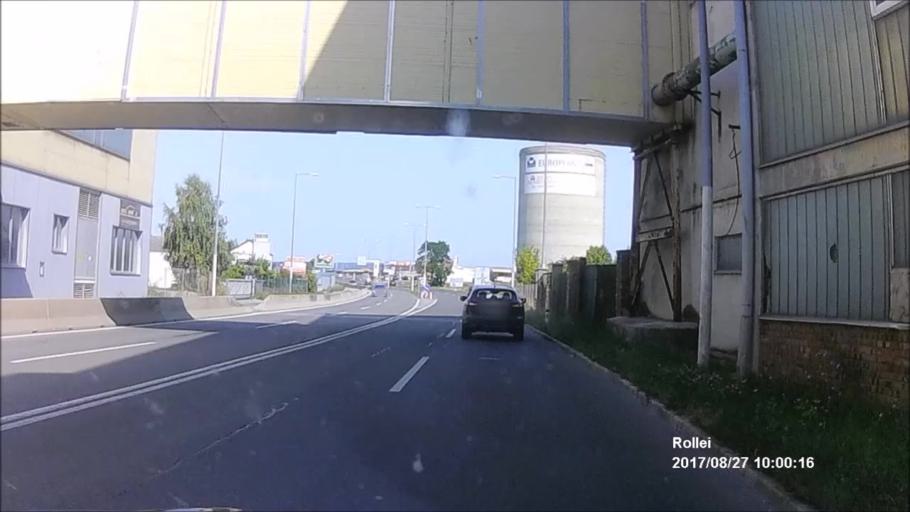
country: AT
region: Burgenland
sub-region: Eisenstadt-Umgebung
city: Zagersdorf
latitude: 47.7704
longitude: 16.5301
